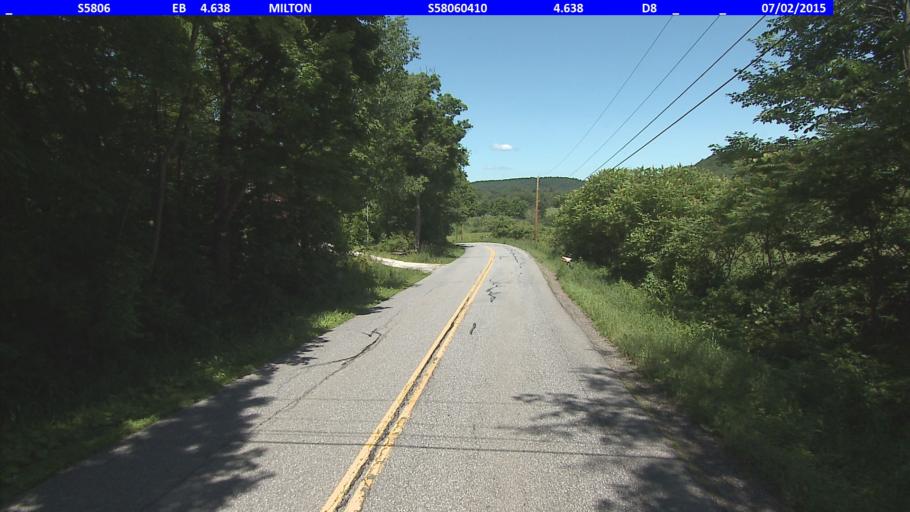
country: US
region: Vermont
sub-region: Chittenden County
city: Milton
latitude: 44.6876
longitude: -73.1770
